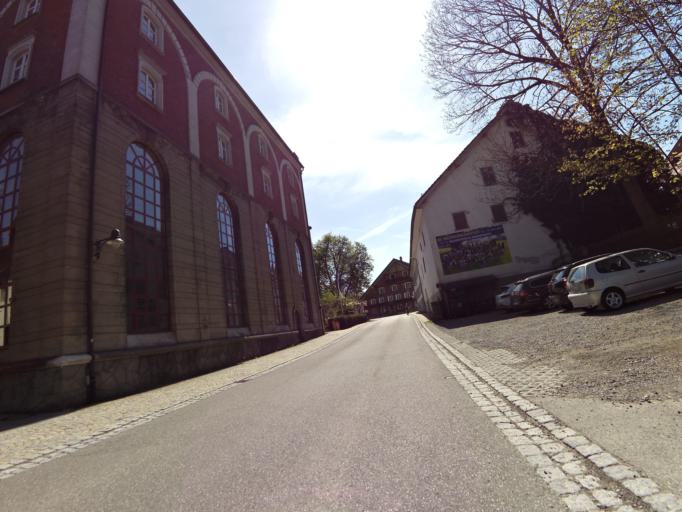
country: DE
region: Bavaria
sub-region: Swabia
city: Oberreute
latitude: 47.5869
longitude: 9.9449
